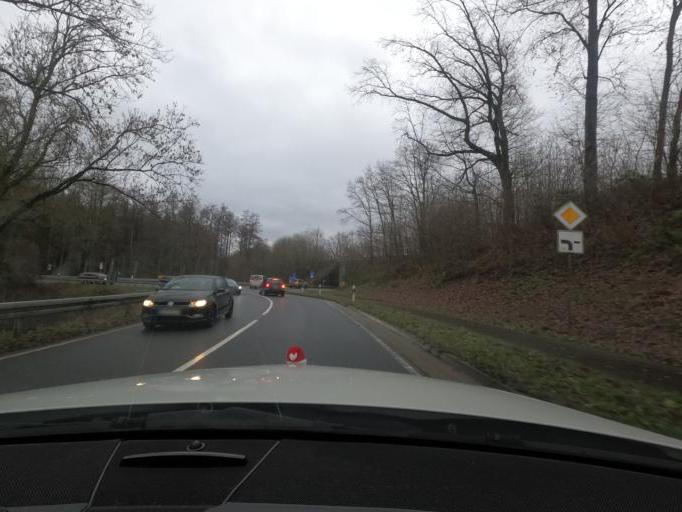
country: DE
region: Lower Saxony
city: Seesen
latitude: 51.8641
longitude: 10.1356
